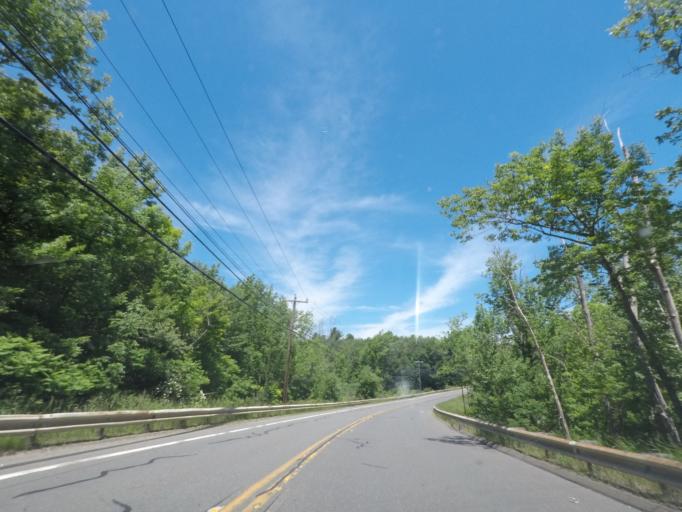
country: US
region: Massachusetts
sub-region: Berkshire County
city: Becket
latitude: 42.2624
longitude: -73.0772
